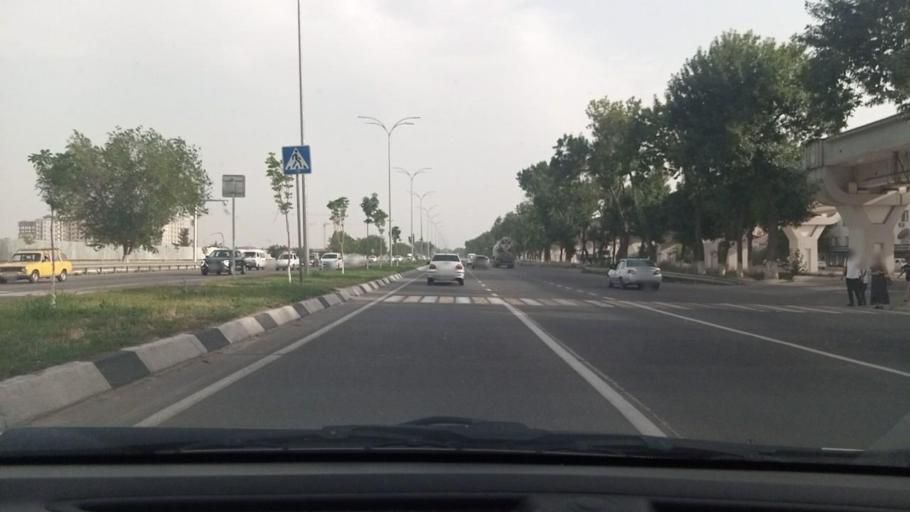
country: UZ
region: Toshkent Shahri
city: Bektemir
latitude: 41.2813
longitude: 69.3608
